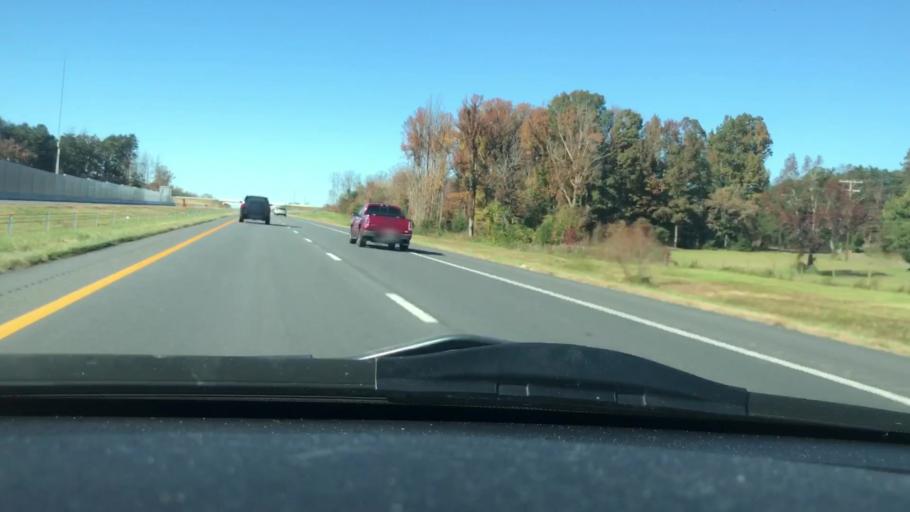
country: US
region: North Carolina
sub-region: Guilford County
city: Summerfield
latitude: 36.2604
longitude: -79.9263
